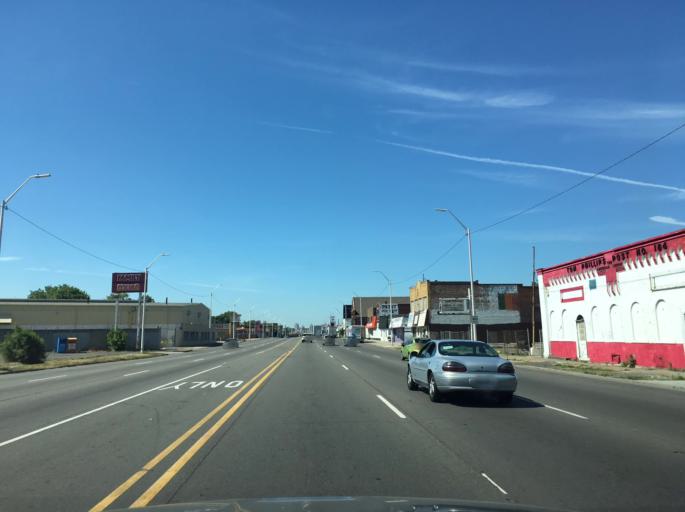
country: US
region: Michigan
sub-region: Wayne County
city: Hamtramck
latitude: 42.3974
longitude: -83.0025
